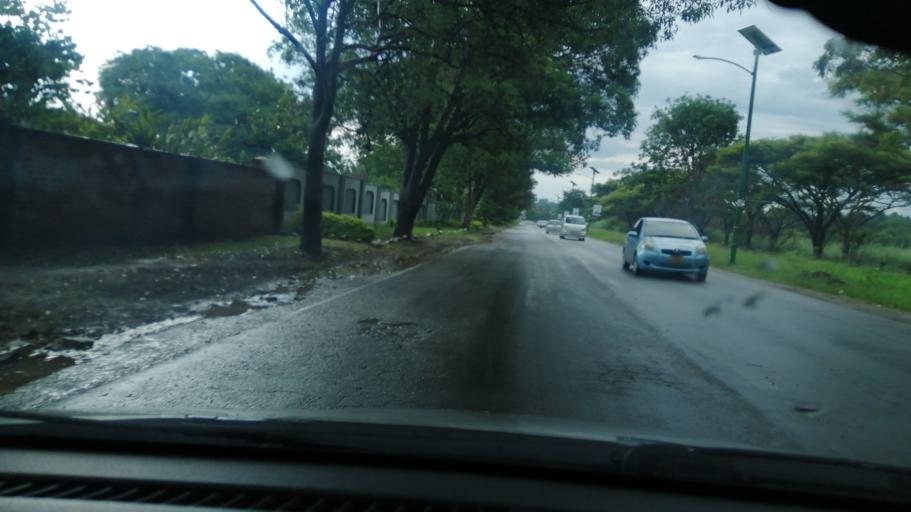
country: ZW
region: Harare
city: Harare
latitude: -17.7902
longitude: 31.0570
